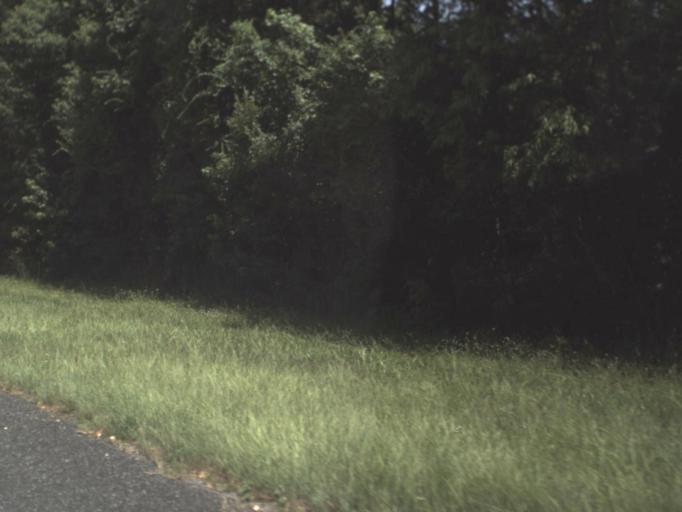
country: US
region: Florida
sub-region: Taylor County
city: Steinhatchee
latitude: 29.6803
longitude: -83.2585
